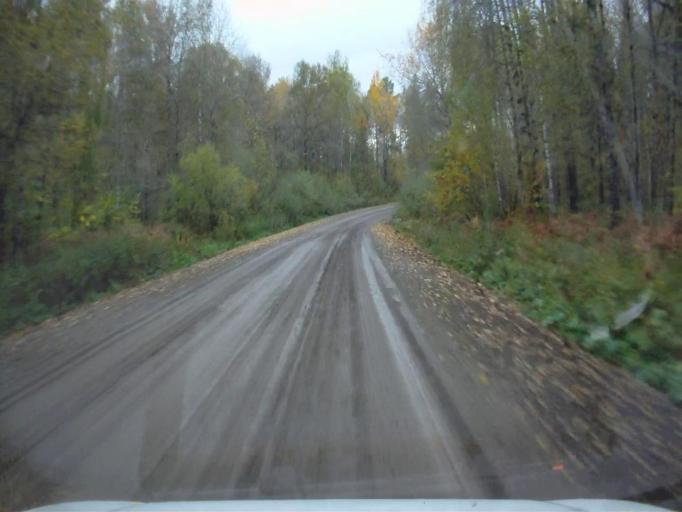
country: RU
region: Chelyabinsk
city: Nyazepetrovsk
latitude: 56.1145
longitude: 59.3683
